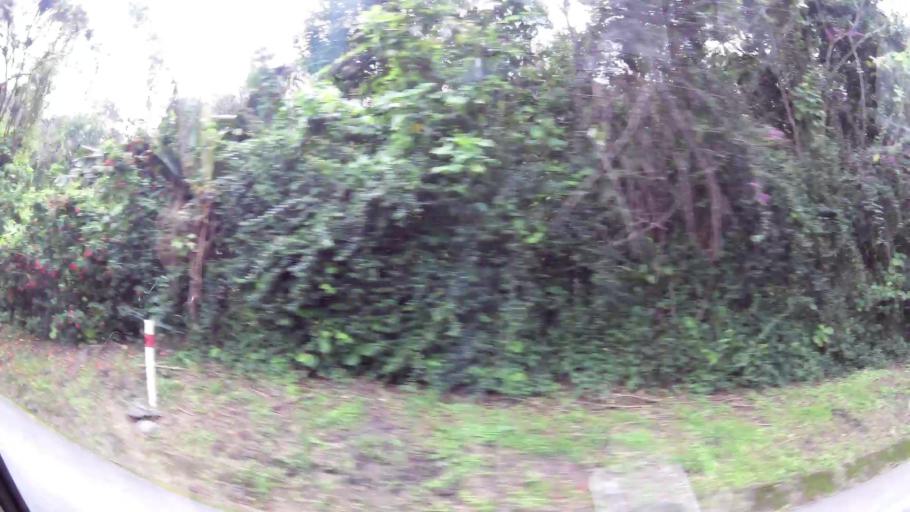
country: EC
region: Santo Domingo de los Tsachilas
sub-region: Canton Santo Domingo de los Colorados
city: Santo Domingo de los Colorados
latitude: -0.2861
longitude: -79.0684
